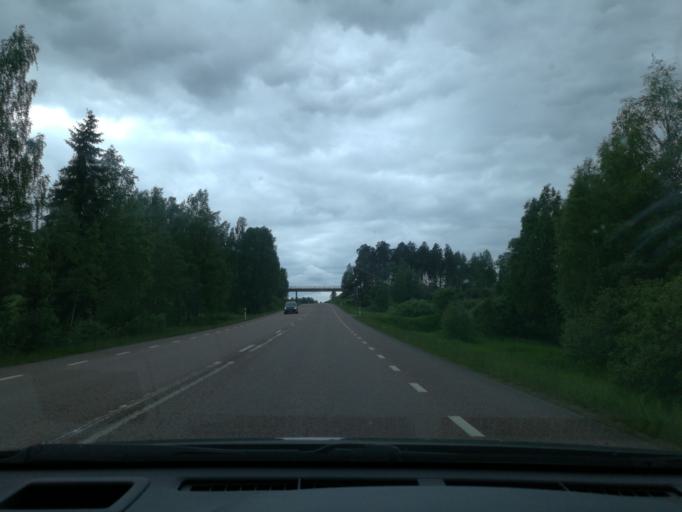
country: SE
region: Dalarna
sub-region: Smedjebackens Kommun
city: Smedjebacken
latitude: 60.1388
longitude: 15.3859
